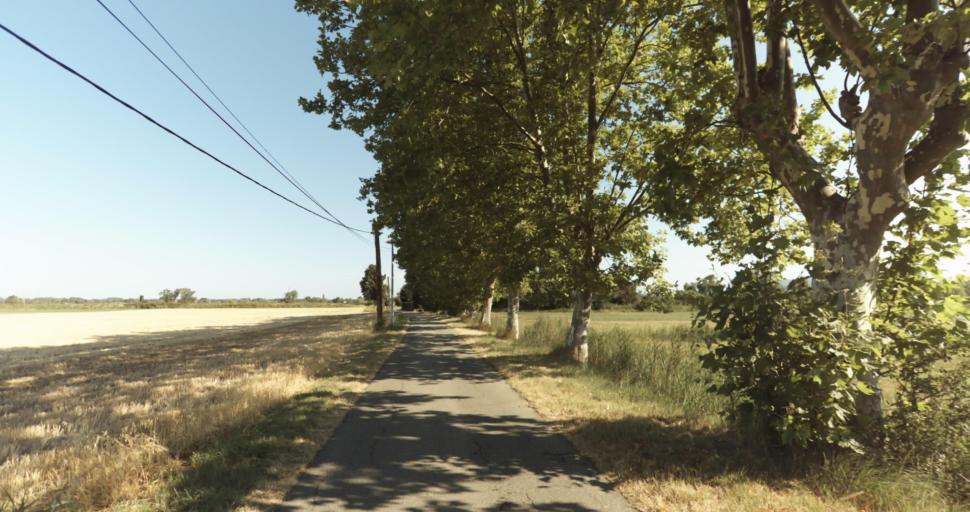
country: FR
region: Provence-Alpes-Cote d'Azur
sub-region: Departement du Vaucluse
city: Sarrians
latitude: 44.0457
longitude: 4.9535
